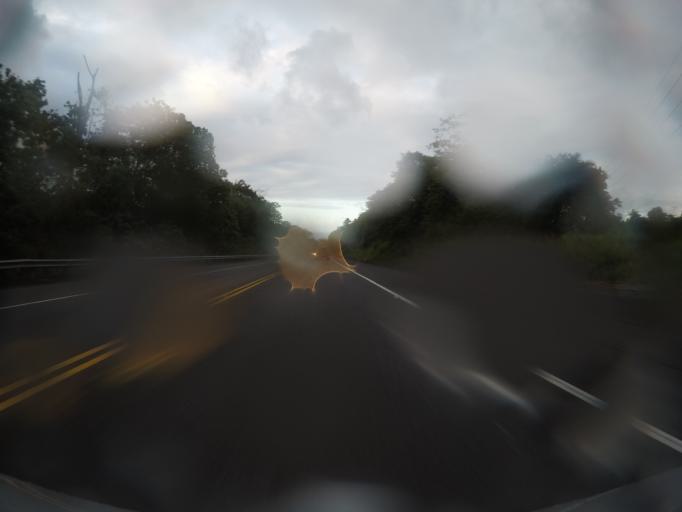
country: US
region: Hawaii
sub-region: Hawaii County
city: Hilo
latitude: 19.6813
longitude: -155.1235
